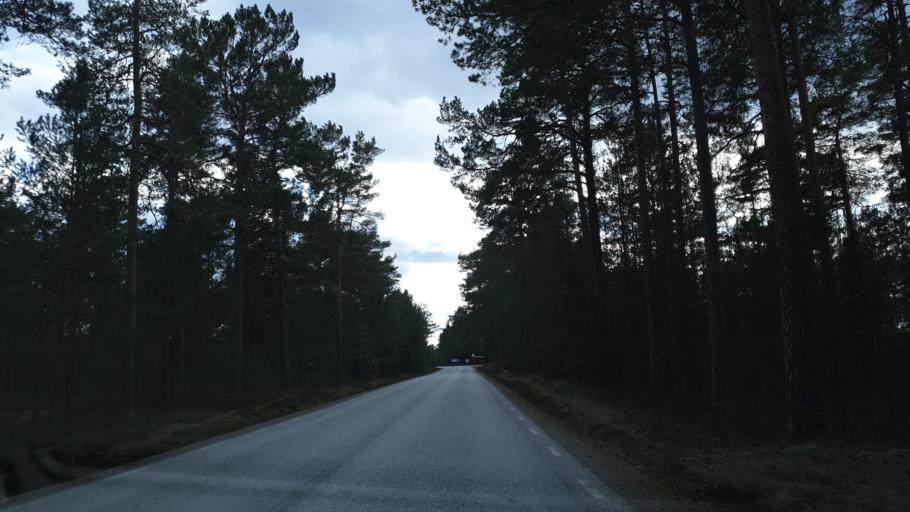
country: SE
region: Stockholm
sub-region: Varmdo Kommun
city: Hemmesta
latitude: 59.2221
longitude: 18.5249
